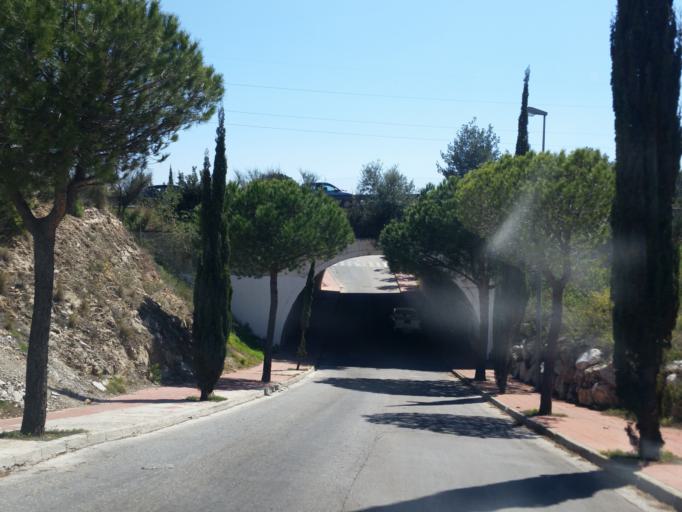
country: ES
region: Andalusia
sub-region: Provincia de Malaga
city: Benalmadena
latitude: 36.6106
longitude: -4.5359
